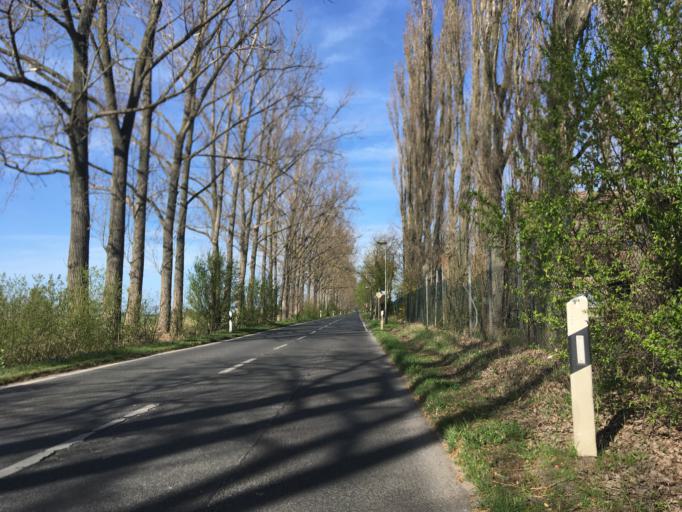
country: DE
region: Berlin
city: Wartenberg
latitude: 52.5841
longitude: 13.5228
